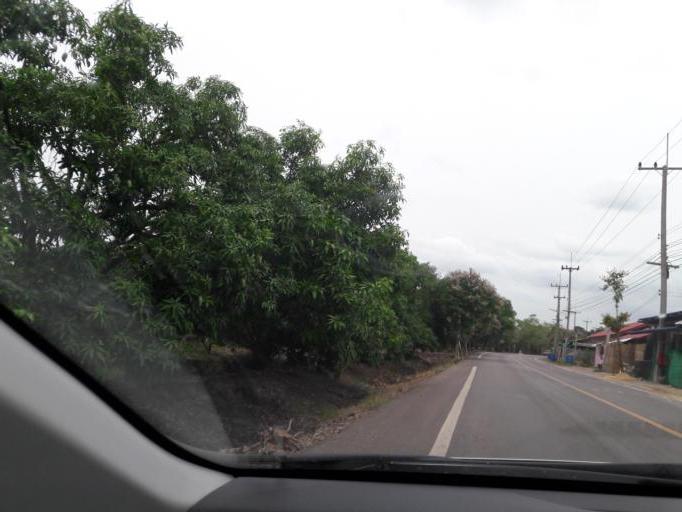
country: TH
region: Samut Sakhon
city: Ban Phaeo
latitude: 13.6196
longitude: 100.0223
